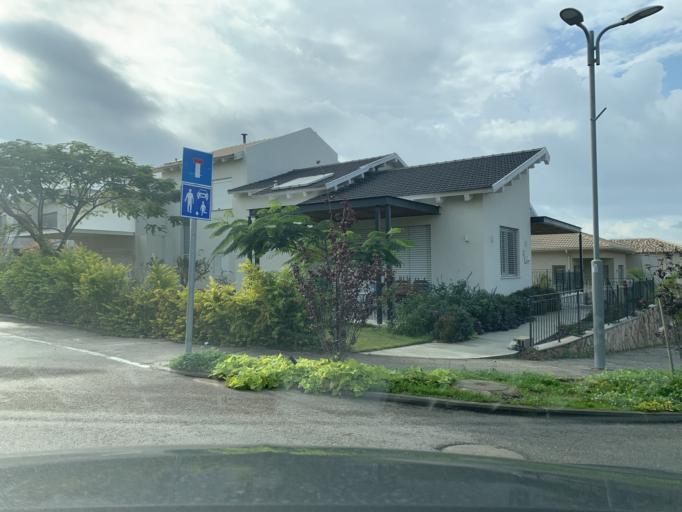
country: IL
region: Central District
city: Rosh Ha'Ayin
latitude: 32.0634
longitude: 34.9509
